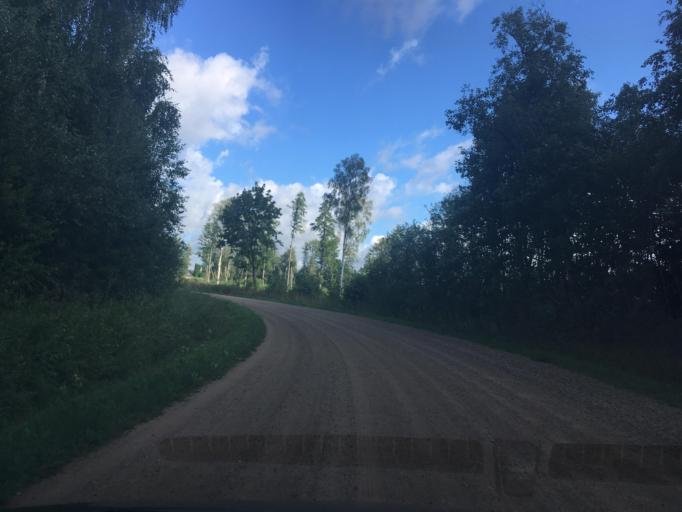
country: EE
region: Jogevamaa
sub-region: Poltsamaa linn
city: Poltsamaa
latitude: 58.4618
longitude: 25.9554
